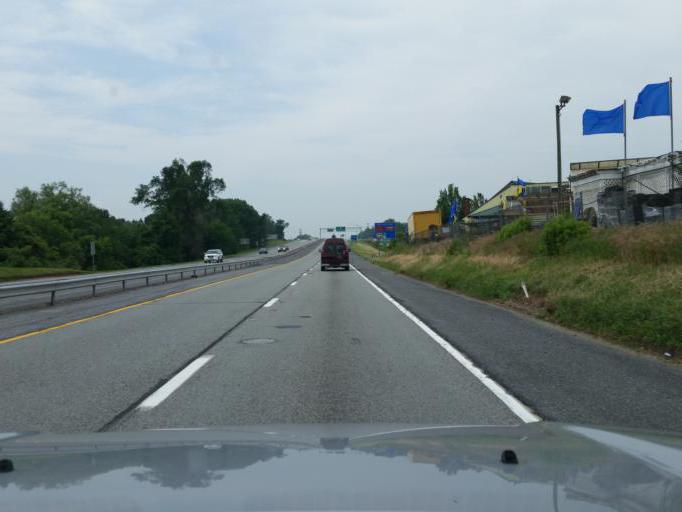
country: US
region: Pennsylvania
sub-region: Cumberland County
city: Mechanicsburg
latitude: 40.1853
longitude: -76.9828
